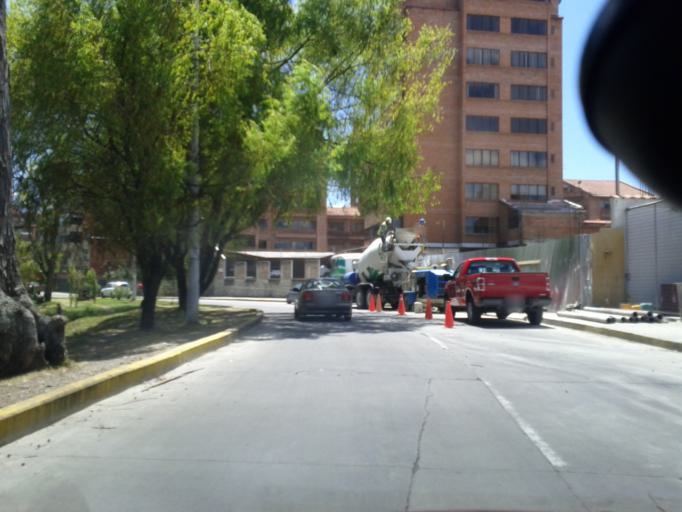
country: EC
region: Azuay
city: Cuenca
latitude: -2.8924
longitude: -79.0208
